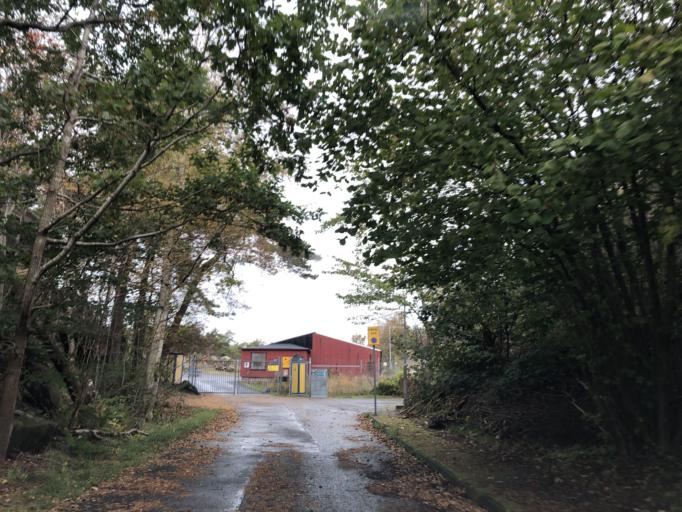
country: SE
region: Vaestra Goetaland
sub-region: Goteborg
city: Majorna
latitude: 57.6729
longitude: 11.8551
